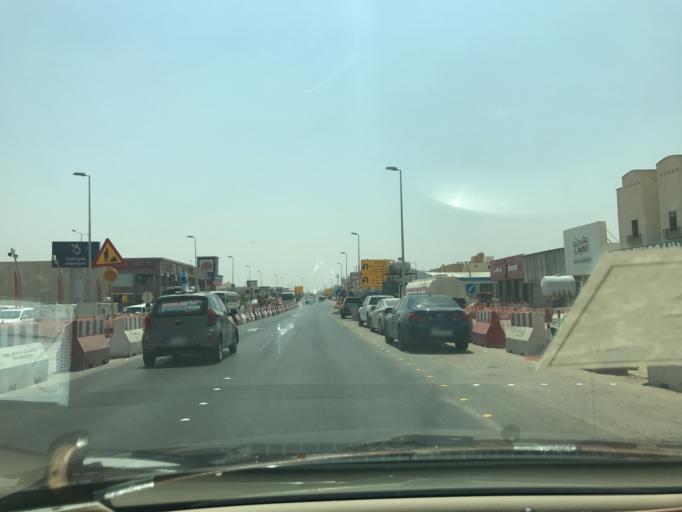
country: SA
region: Ar Riyad
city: Riyadh
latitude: 24.7509
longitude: 46.7717
